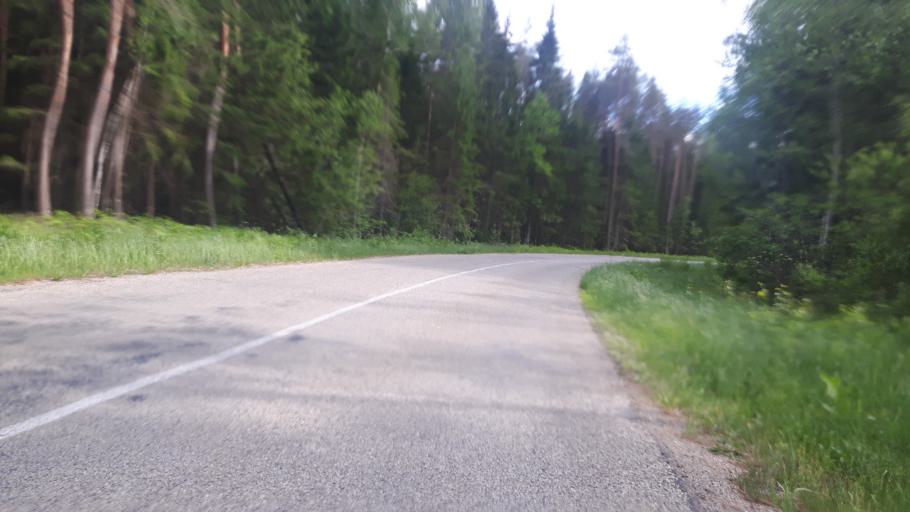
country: LV
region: Engure
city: Smarde
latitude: 57.0129
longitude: 23.3422
